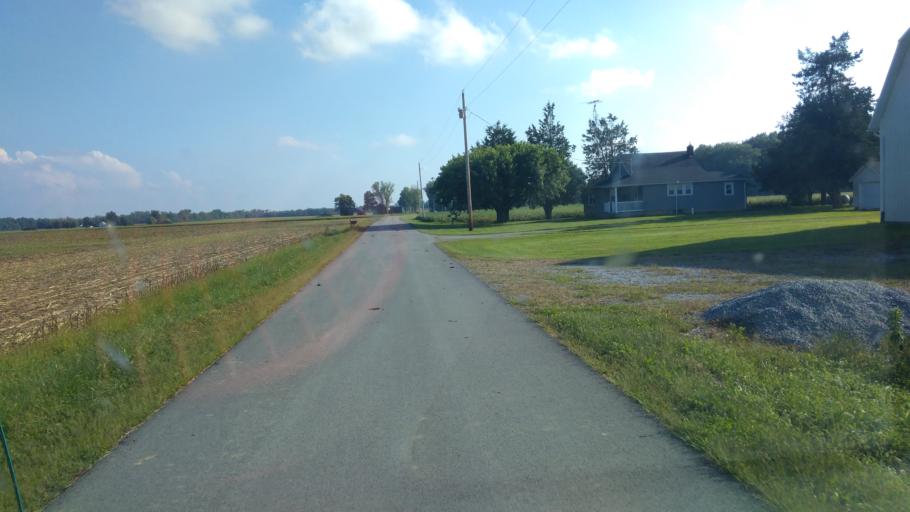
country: US
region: Ohio
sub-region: Hardin County
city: Forest
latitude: 40.7329
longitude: -83.4776
